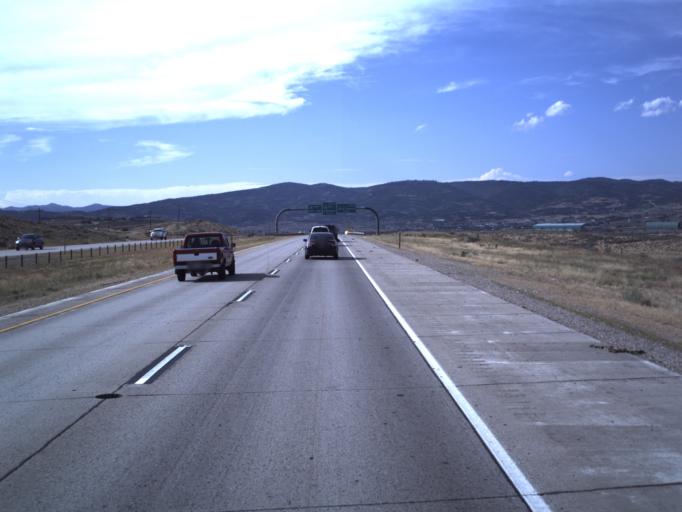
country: US
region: Utah
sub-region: Summit County
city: Park City
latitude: 40.7051
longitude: -111.4770
